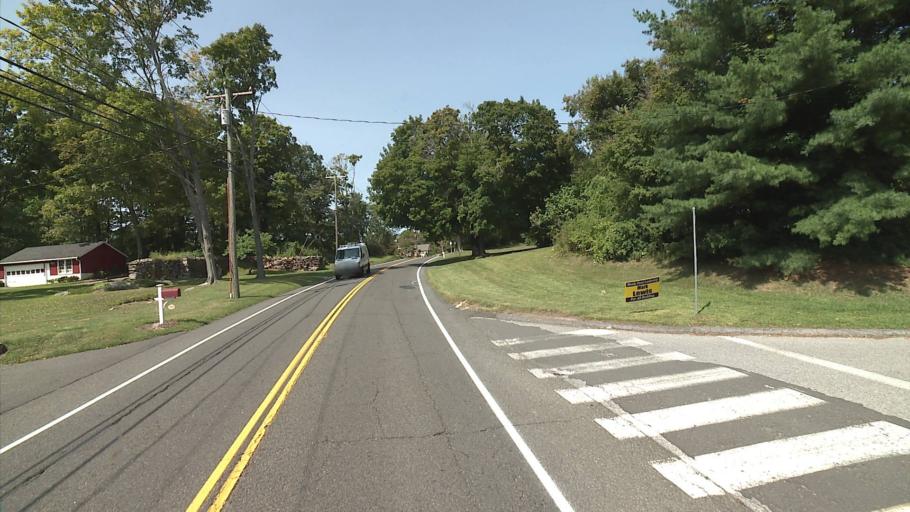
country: US
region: Connecticut
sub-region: Fairfield County
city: Georgetown
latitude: 41.2983
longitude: -73.3444
